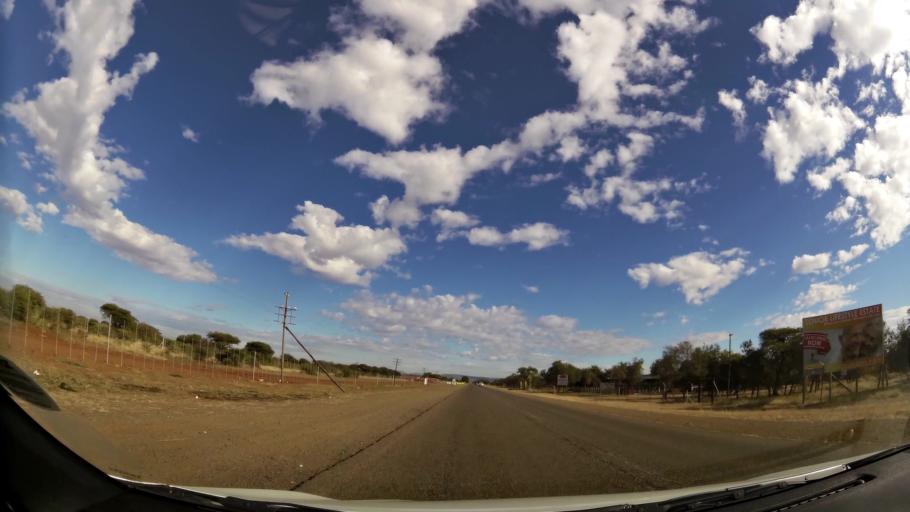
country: ZA
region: Limpopo
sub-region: Waterberg District Municipality
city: Bela-Bela
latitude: -24.9158
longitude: 28.3649
